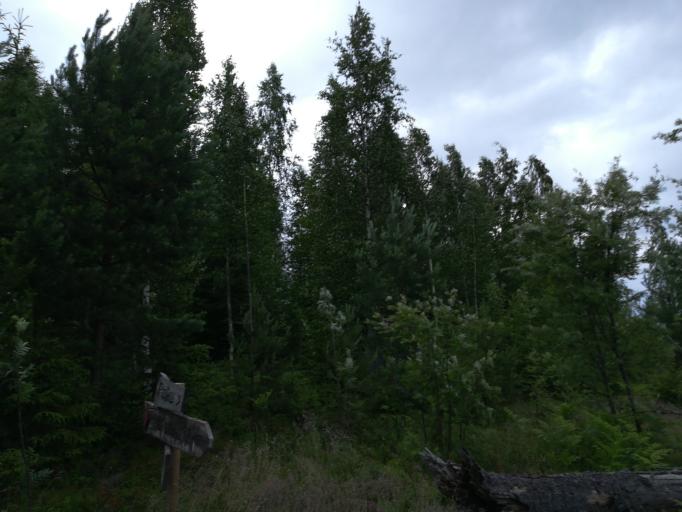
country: FI
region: South Karelia
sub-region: Lappeenranta
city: Savitaipale
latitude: 61.1840
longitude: 27.5564
